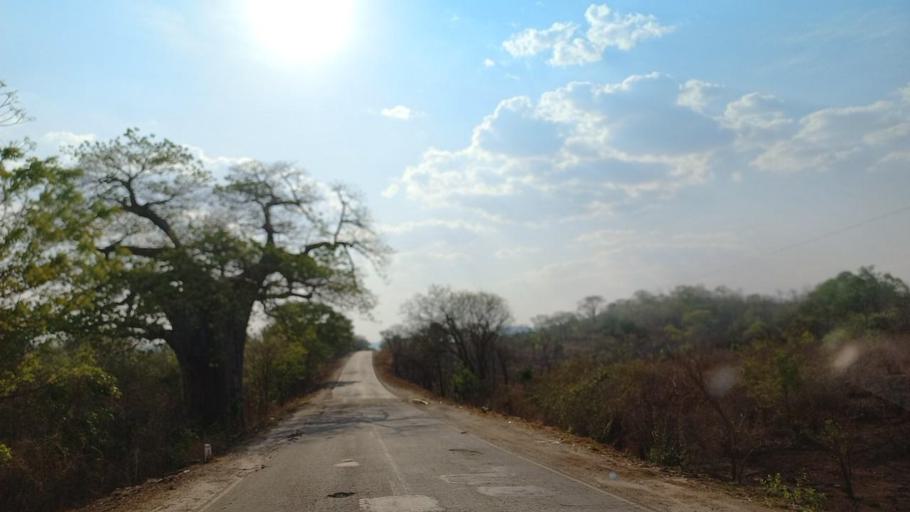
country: ZM
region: Lusaka
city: Luangwa
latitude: -14.9821
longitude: 30.1386
